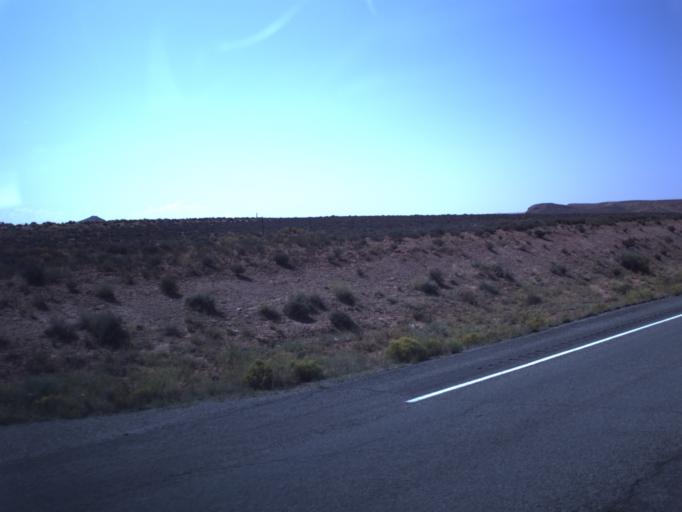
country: US
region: Utah
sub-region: San Juan County
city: Blanding
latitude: 37.0174
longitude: -109.6096
